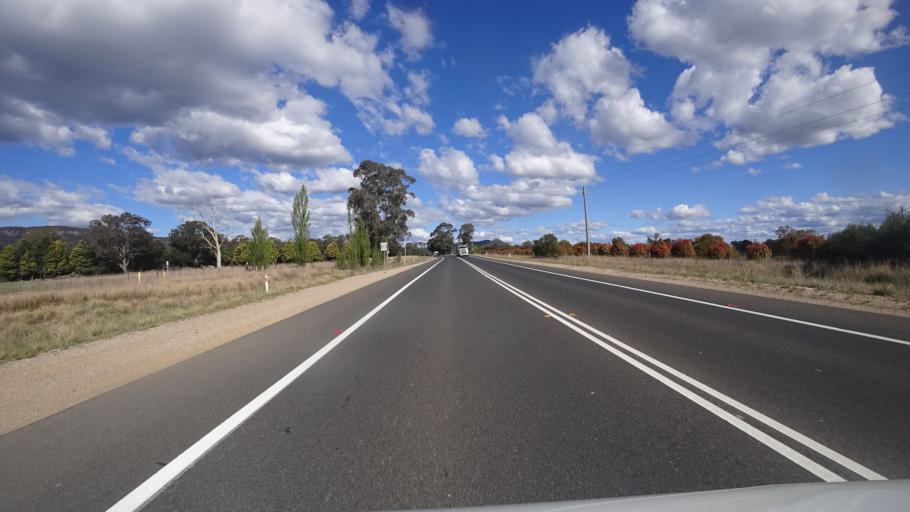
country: AU
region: New South Wales
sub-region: Lithgow
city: Bowenfels
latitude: -33.5547
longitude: 150.1905
